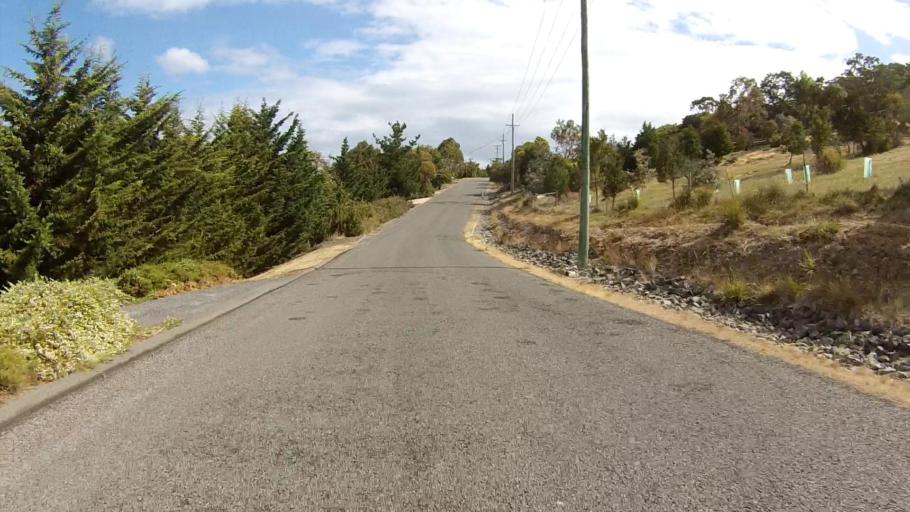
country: AU
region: Tasmania
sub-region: Clarence
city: Acton Park
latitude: -42.8823
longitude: 147.5039
